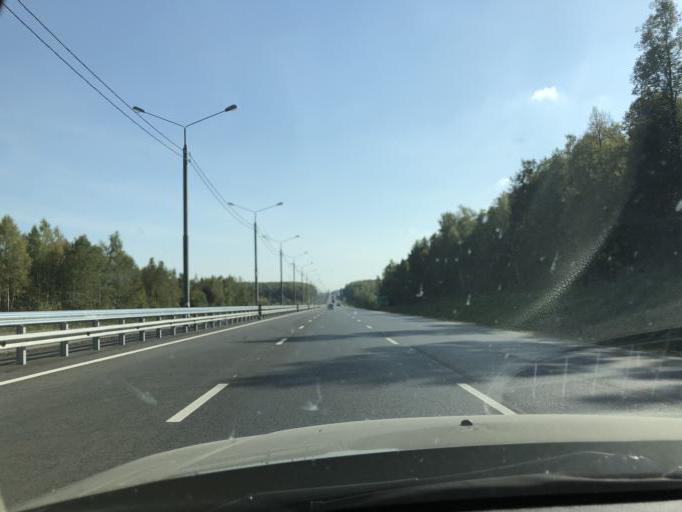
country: RU
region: Tula
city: Zaokskiy
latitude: 54.6093
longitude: 37.4973
